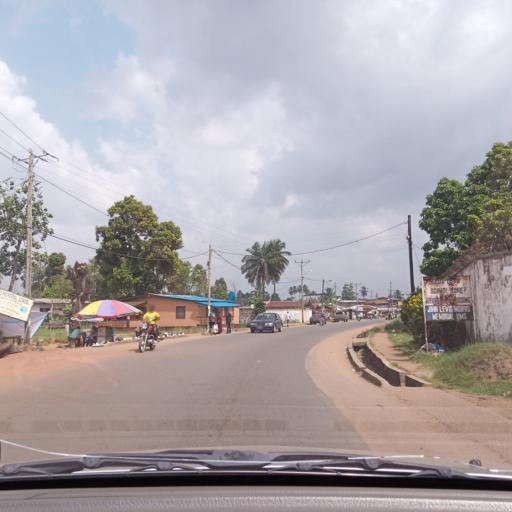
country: LR
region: Montserrado
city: Monrovia
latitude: 6.2743
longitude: -10.6949
